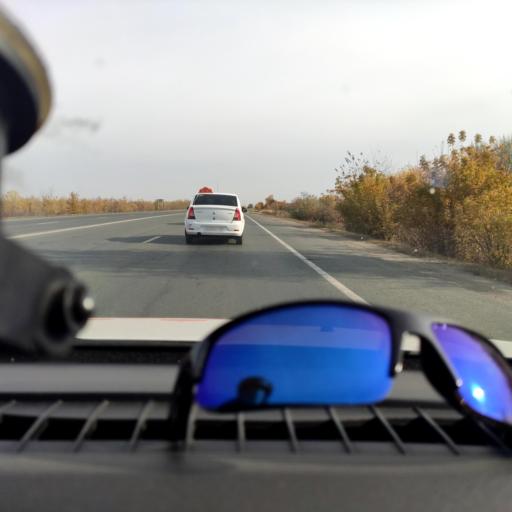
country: RU
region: Samara
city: Novokuybyshevsk
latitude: 53.0768
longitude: 50.0395
